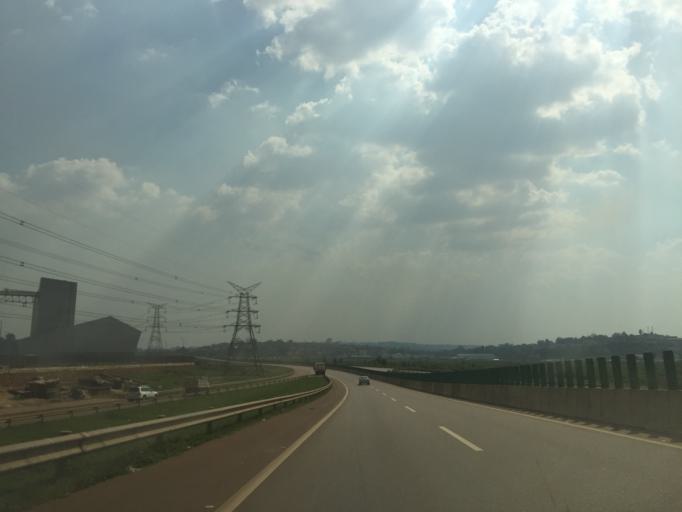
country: UG
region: Central Region
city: Kampala Central Division
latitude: 0.3095
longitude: 32.5141
